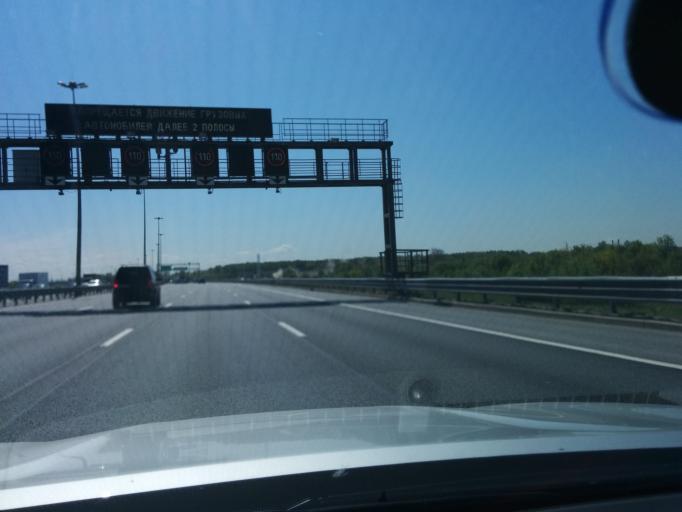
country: RU
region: St.-Petersburg
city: Krasnogvargeisky
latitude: 60.0029
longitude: 30.4761
